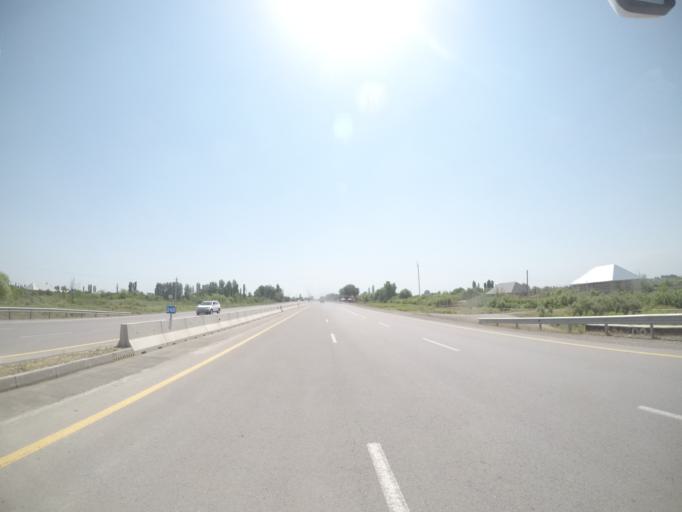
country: AZ
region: Agdas
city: Agdas
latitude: 40.5406
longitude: 47.4160
